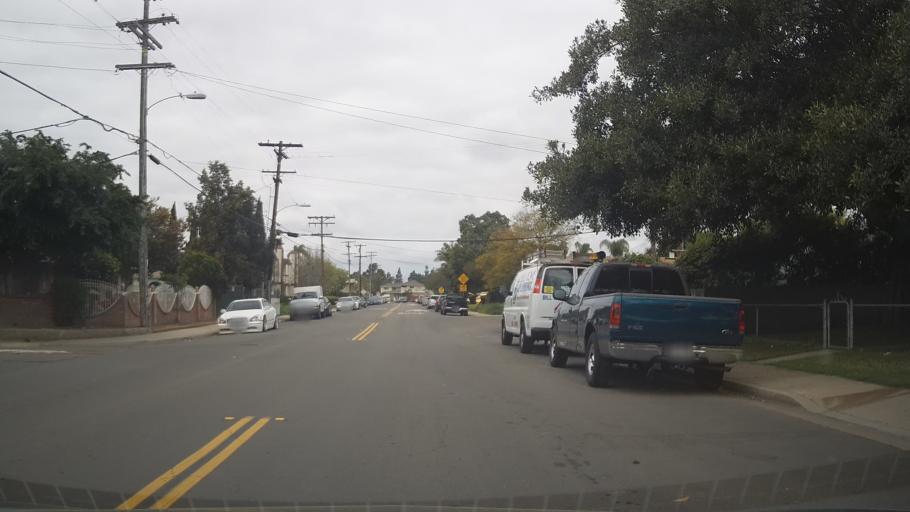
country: US
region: California
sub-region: San Diego County
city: La Mesa
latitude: 32.7676
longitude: -117.0509
